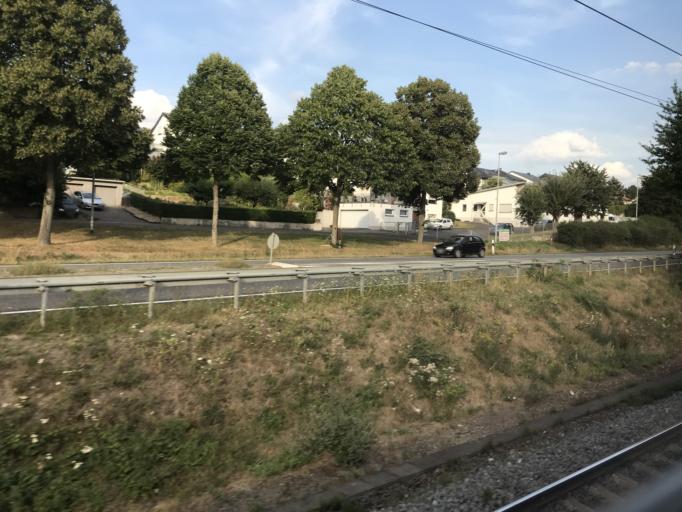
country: DE
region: Hesse
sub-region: Regierungsbezirk Giessen
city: Villmar
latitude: 50.3575
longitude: 8.1823
